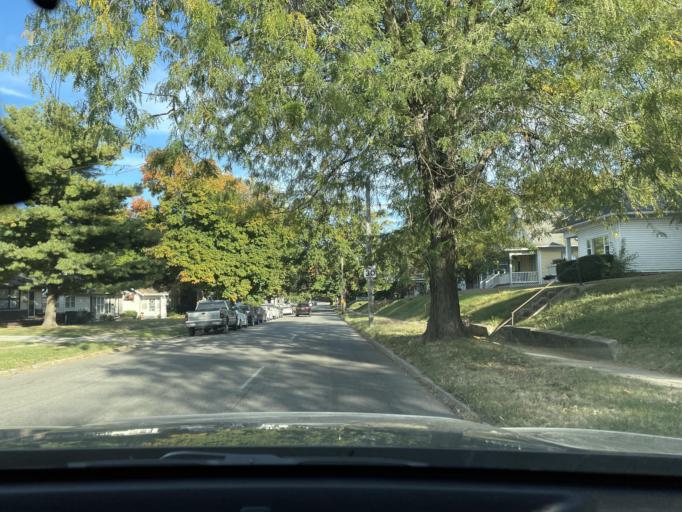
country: US
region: Missouri
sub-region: Buchanan County
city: Saint Joseph
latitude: 39.7683
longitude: -94.8192
